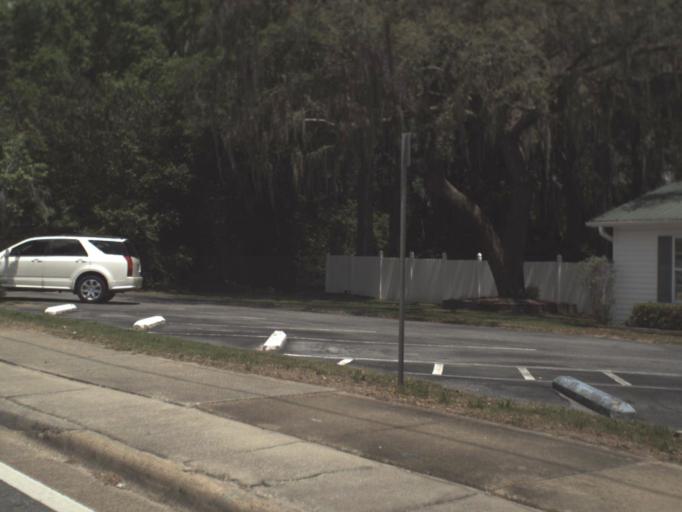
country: US
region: Florida
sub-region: Santa Rosa County
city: Milton
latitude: 30.6407
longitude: -87.0429
